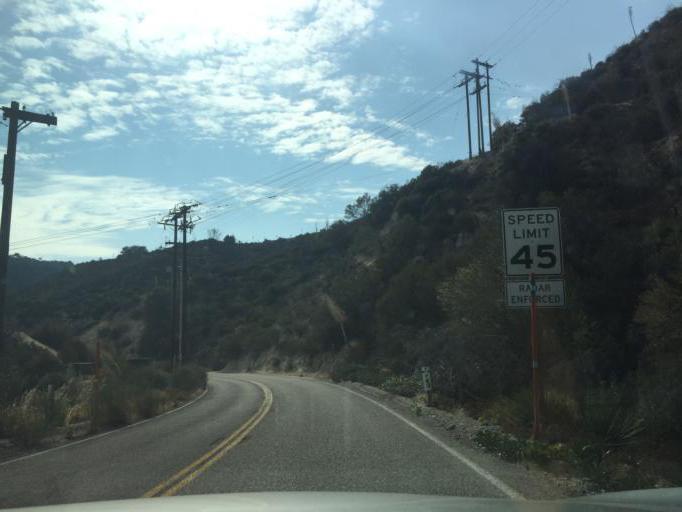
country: US
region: California
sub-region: Los Angeles County
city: Altadena
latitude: 34.2609
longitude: -118.1021
